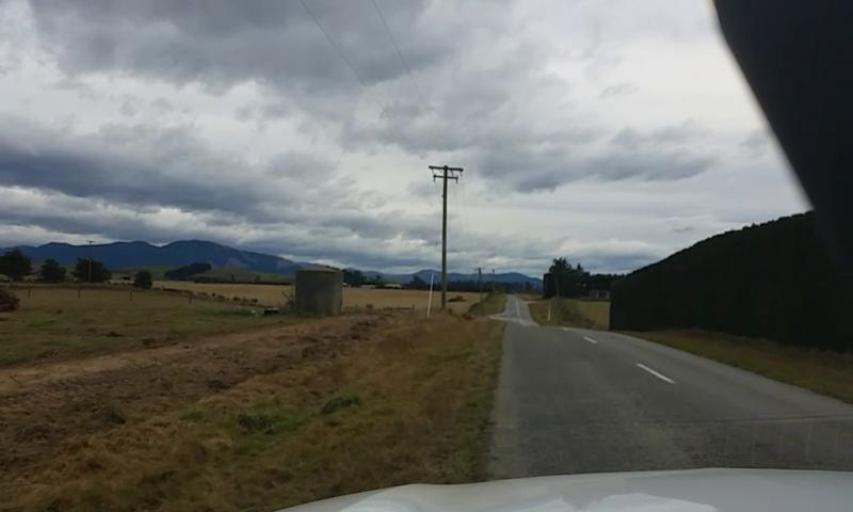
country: NZ
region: Canterbury
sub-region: Waimakariri District
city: Kaiapoi
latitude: -43.2931
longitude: 172.4375
